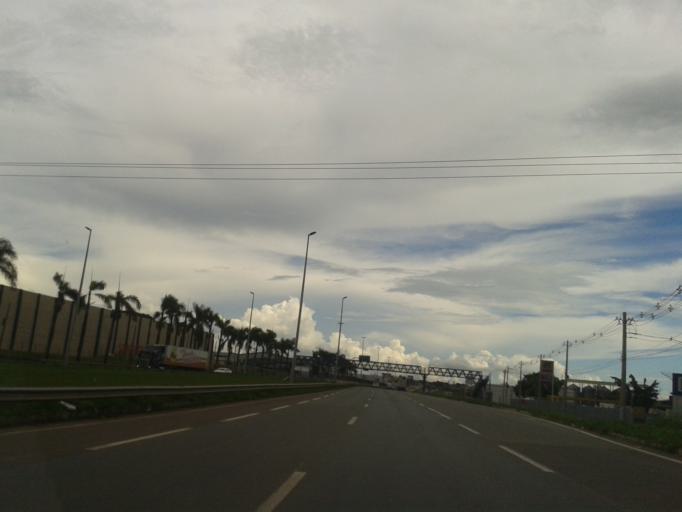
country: BR
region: Goias
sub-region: Aparecida De Goiania
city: Aparecida de Goiania
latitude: -16.8022
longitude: -49.2392
